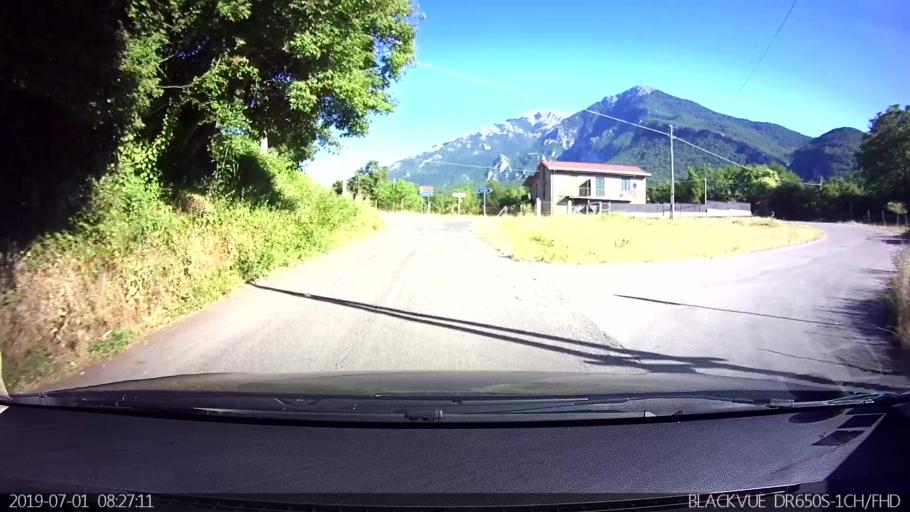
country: IT
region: Latium
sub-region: Provincia di Frosinone
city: Collepardo
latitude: 41.7733
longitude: 13.4023
